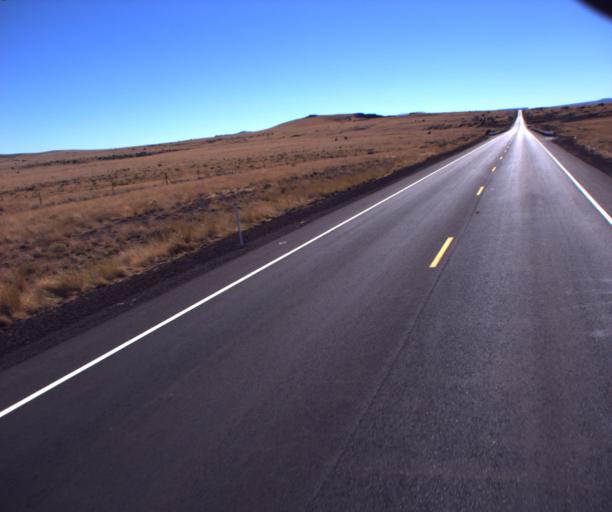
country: US
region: Arizona
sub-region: Apache County
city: Springerville
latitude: 34.2592
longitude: -109.3556
